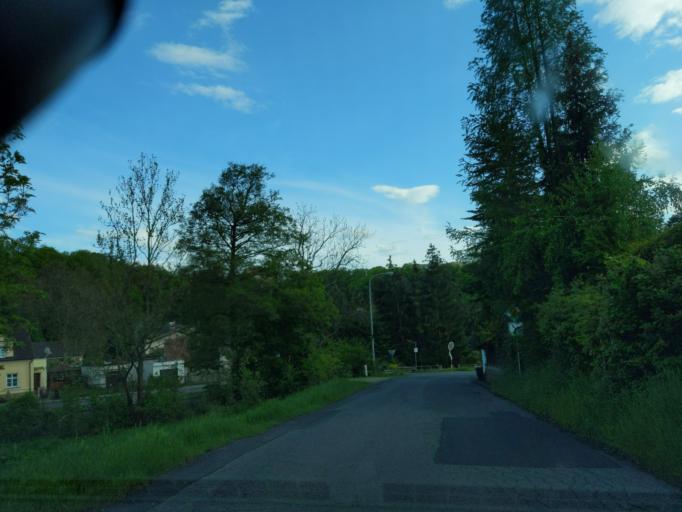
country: CZ
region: Ustecky
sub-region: Okres Usti nad Labem
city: Usti nad Labem
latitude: 50.6873
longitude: 14.0204
